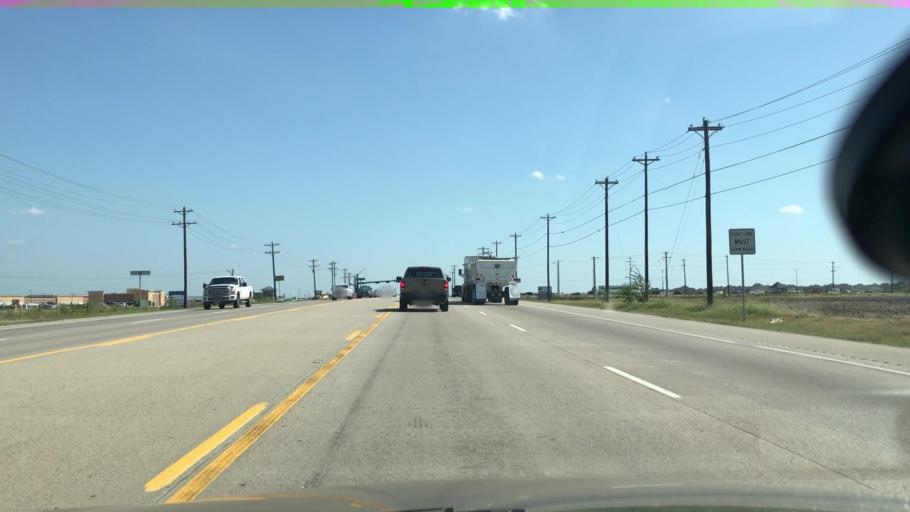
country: US
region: Texas
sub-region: Denton County
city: Little Elm
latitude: 33.2192
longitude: -96.8837
